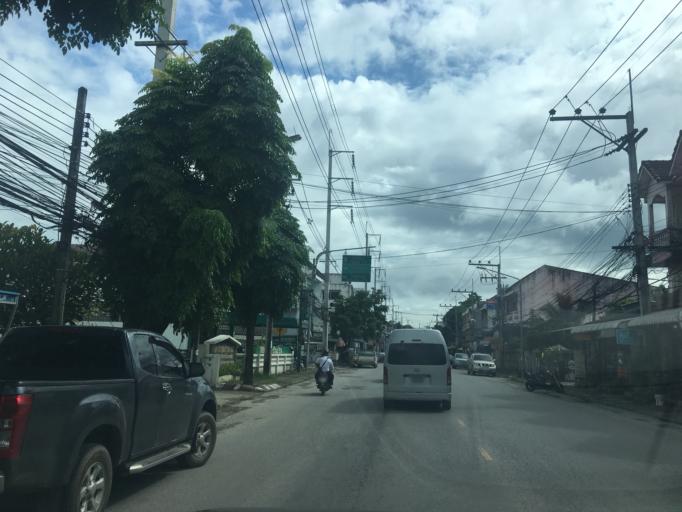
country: TH
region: Chiang Rai
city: Chiang Rai
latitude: 19.9025
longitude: 99.8148
